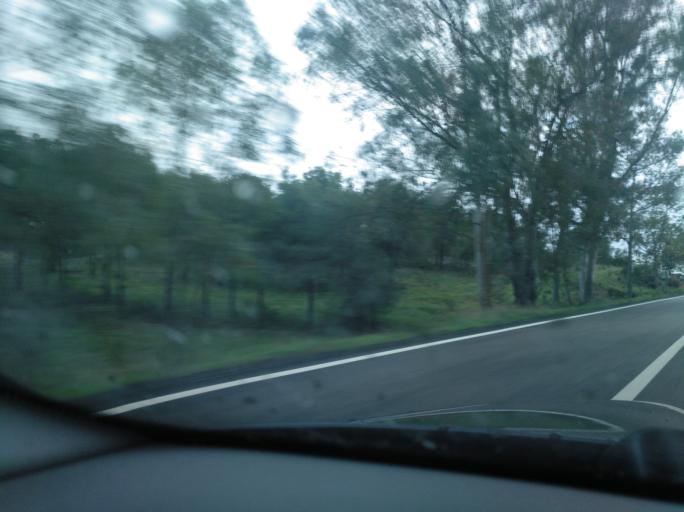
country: PT
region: Faro
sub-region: Alcoutim
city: Alcoutim
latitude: 37.4905
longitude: -7.5732
